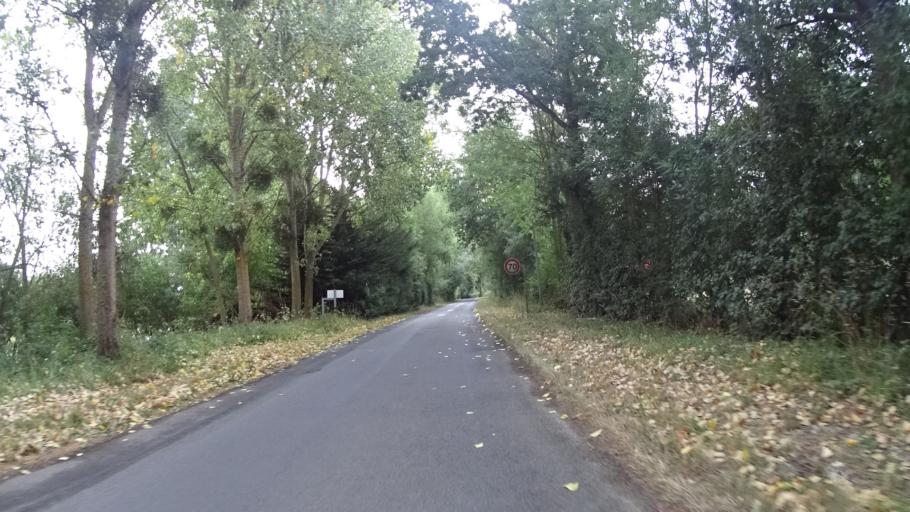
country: FR
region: Pays de la Loire
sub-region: Departement de la Loire-Atlantique
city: Anetz
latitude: 47.3654
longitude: -1.1074
